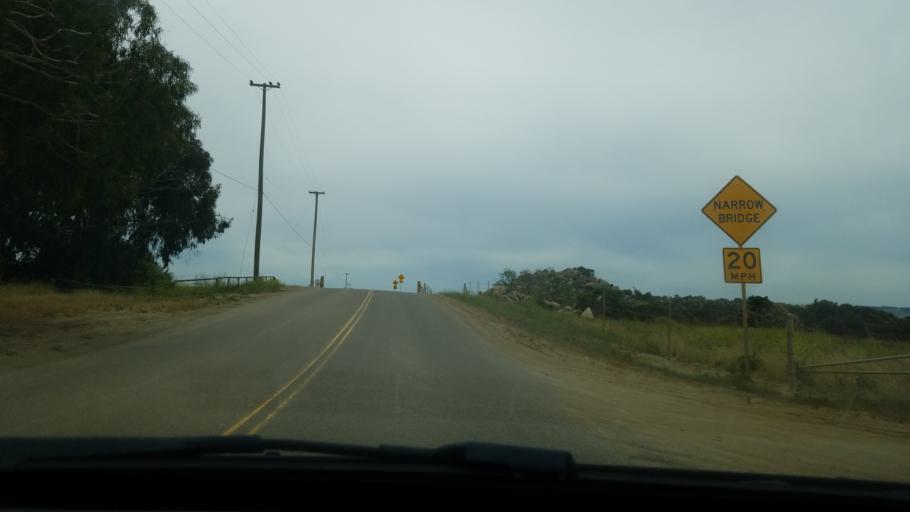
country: US
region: California
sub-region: Santa Barbara County
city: Guadalupe
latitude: 34.9879
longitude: -120.5139
